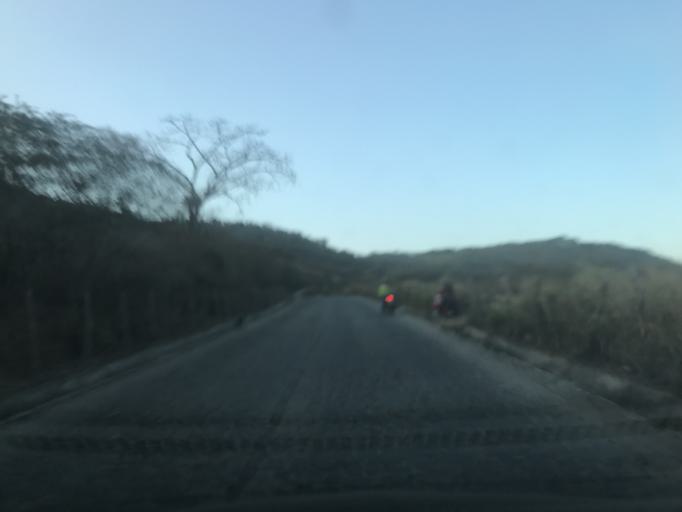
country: BR
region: Pernambuco
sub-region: Bezerros
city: Bezerros
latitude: -8.1897
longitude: -35.7615
